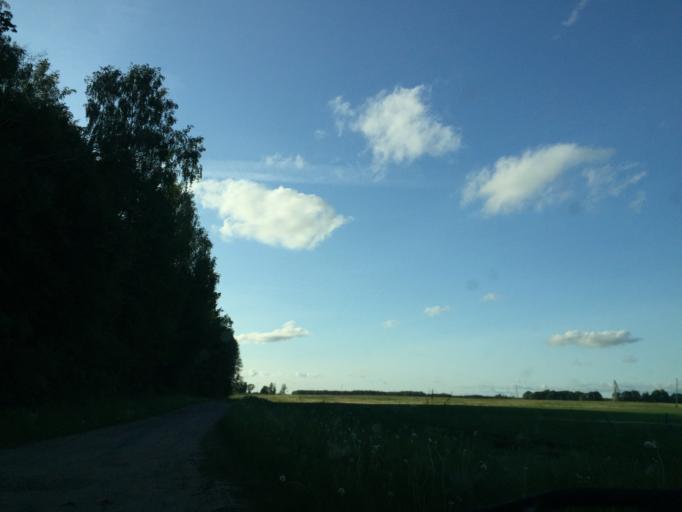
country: LV
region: Koceni
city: Koceni
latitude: 57.4787
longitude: 25.2555
